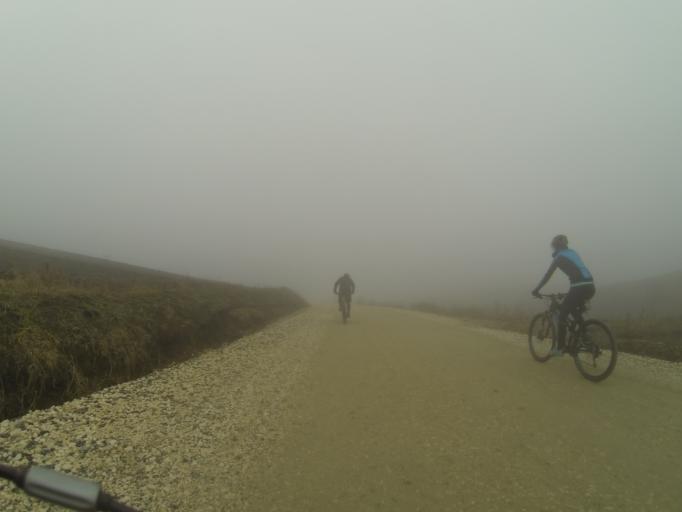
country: RO
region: Mehedinti
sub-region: Comuna Balacita
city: Gvardinita
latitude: 44.4235
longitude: 23.1310
